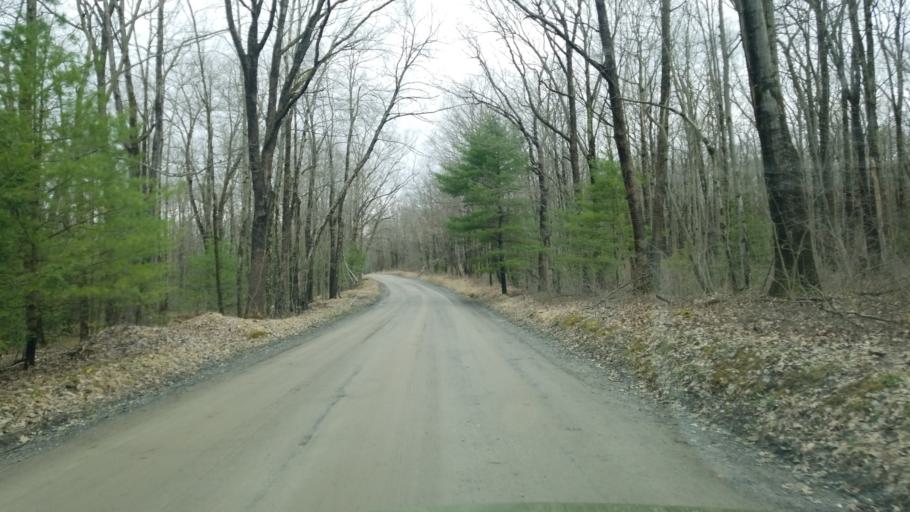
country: US
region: Pennsylvania
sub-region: Clearfield County
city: Shiloh
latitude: 41.1726
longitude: -78.3430
